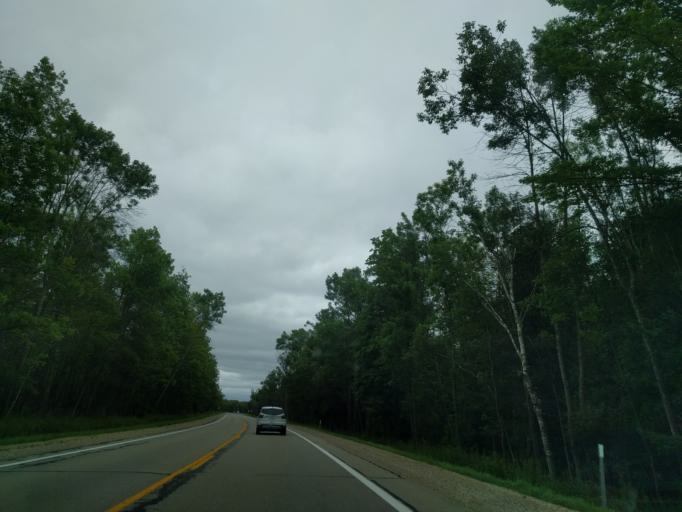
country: US
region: Michigan
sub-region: Menominee County
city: Menominee
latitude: 45.4257
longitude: -87.3509
